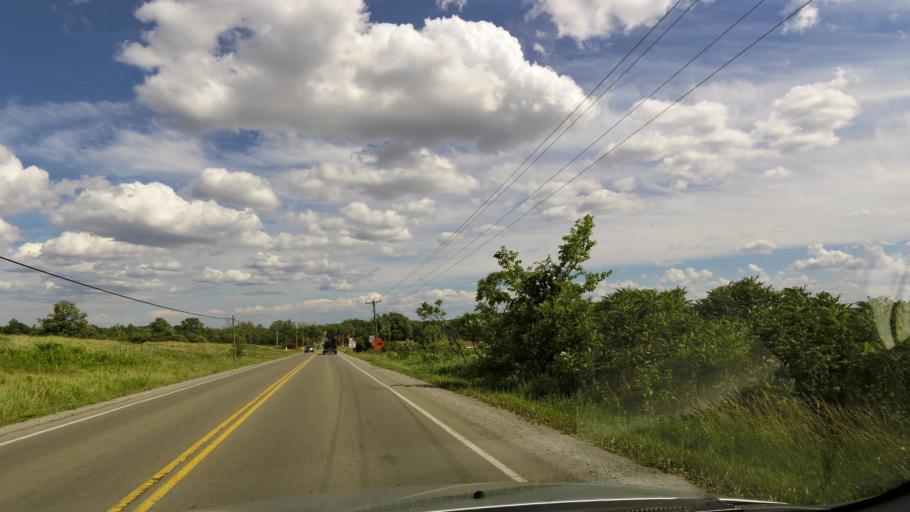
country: CA
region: Ontario
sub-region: Halton
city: Milton
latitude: 43.4649
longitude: -79.9020
